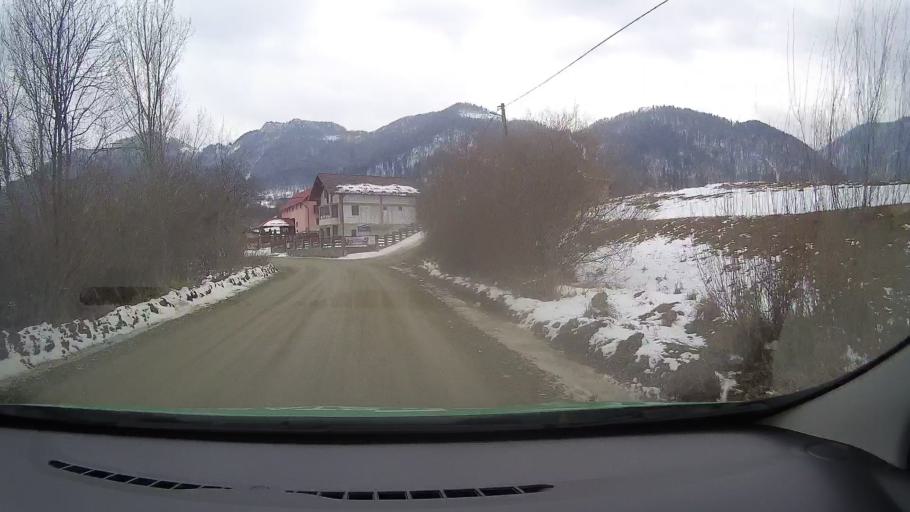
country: RO
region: Brasov
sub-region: Comuna Zarnesti
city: Zarnesti
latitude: 45.5453
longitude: 25.3223
